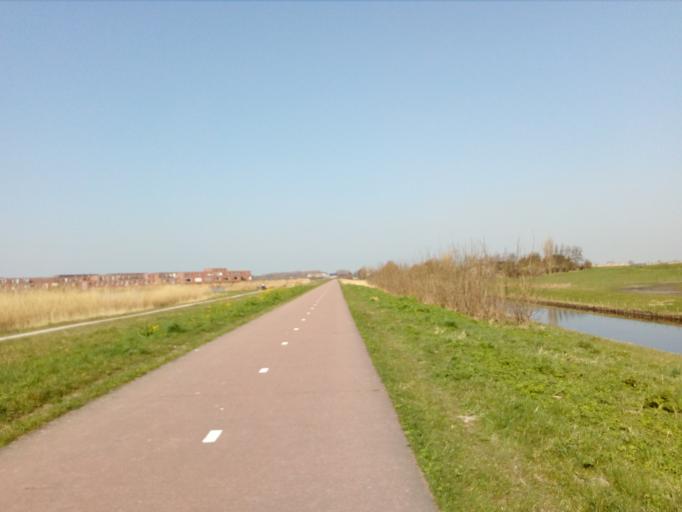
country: NL
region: South Holland
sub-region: Gemeente Rijnwoude
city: Benthuizen
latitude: 52.0779
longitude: 4.5334
